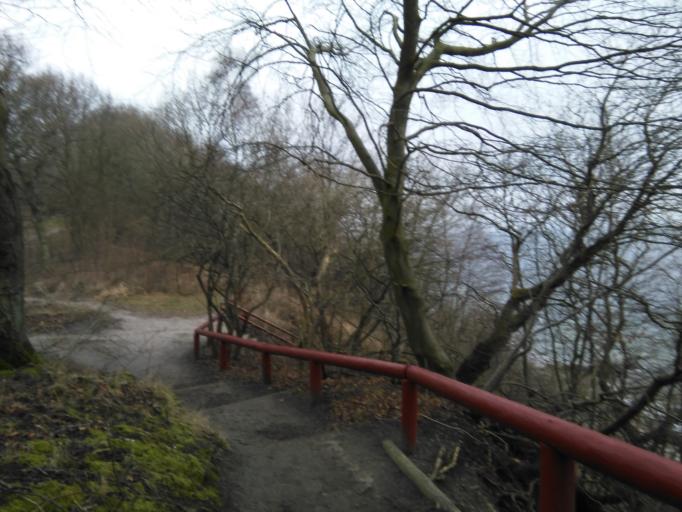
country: DK
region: Central Jutland
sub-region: Arhus Kommune
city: Arhus
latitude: 56.1124
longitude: 10.2317
